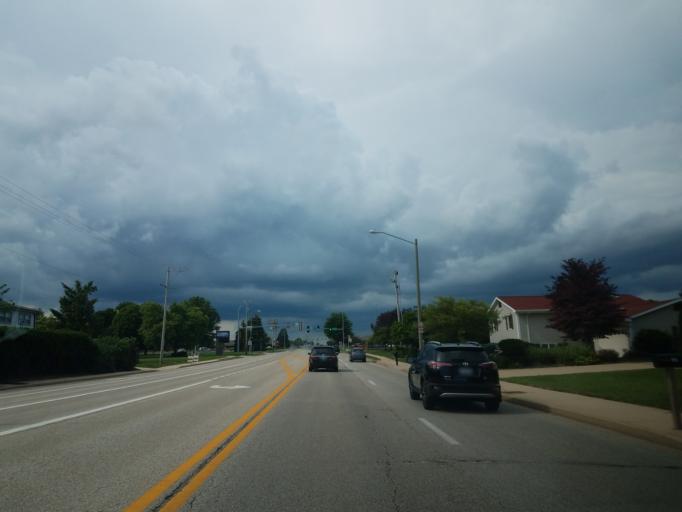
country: US
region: Illinois
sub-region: McLean County
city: Bloomington
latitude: 40.4803
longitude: -88.9432
